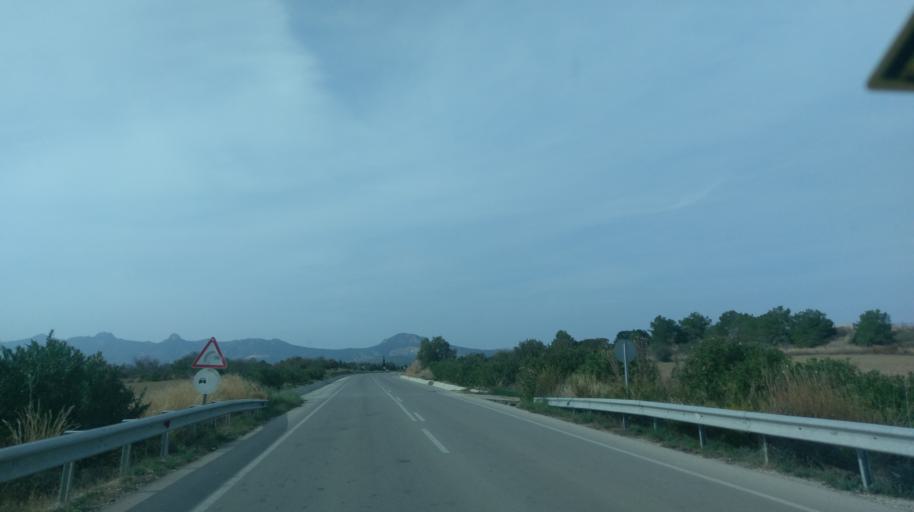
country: CY
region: Ammochostos
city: Leonarisso
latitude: 35.3853
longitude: 34.0142
